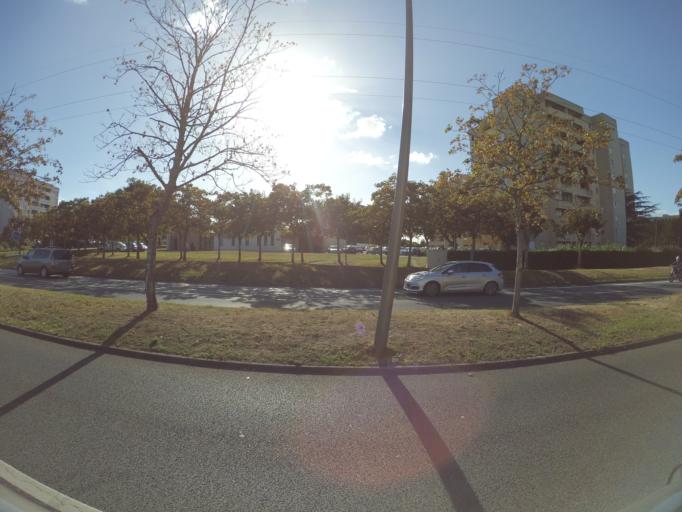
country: FR
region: Pays de la Loire
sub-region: Departement de Maine-et-Loire
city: Cholet
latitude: 47.0491
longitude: -0.8978
